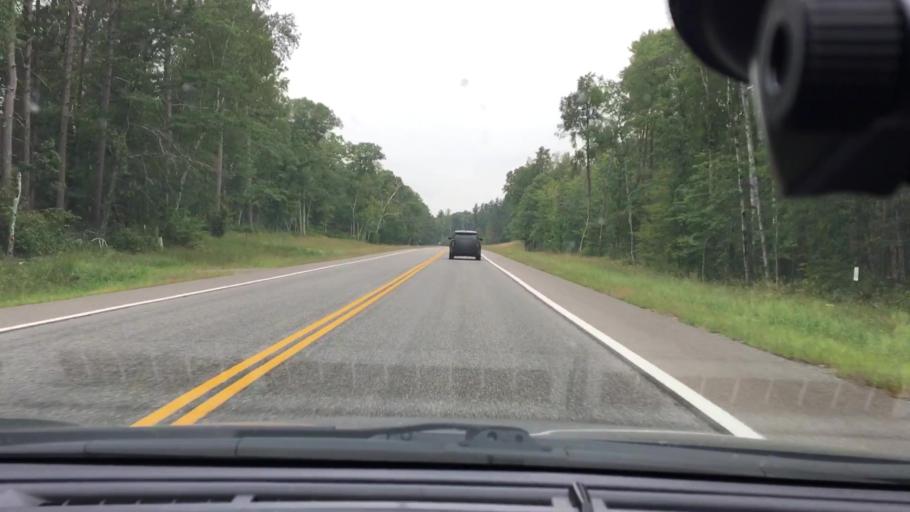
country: US
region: Minnesota
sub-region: Crow Wing County
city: Cross Lake
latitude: 46.6624
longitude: -94.0362
